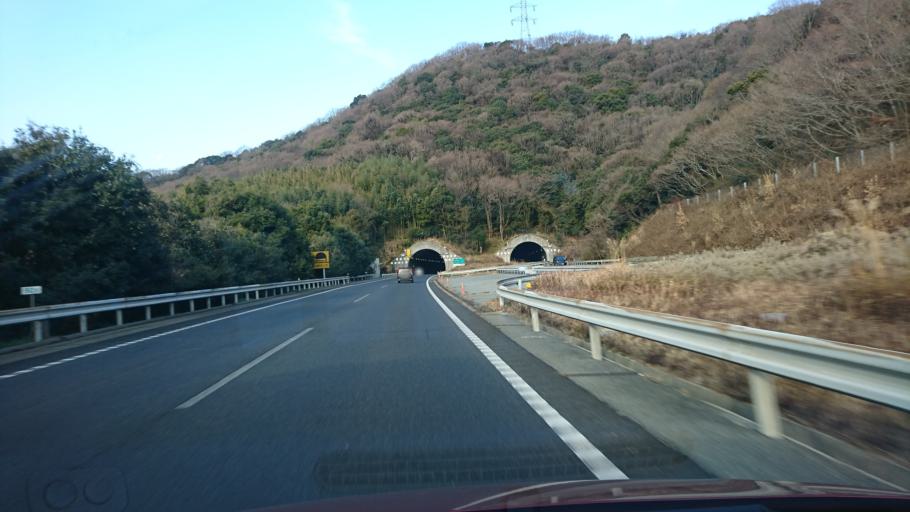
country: JP
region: Hyogo
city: Himeji
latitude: 34.8526
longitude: 134.7334
